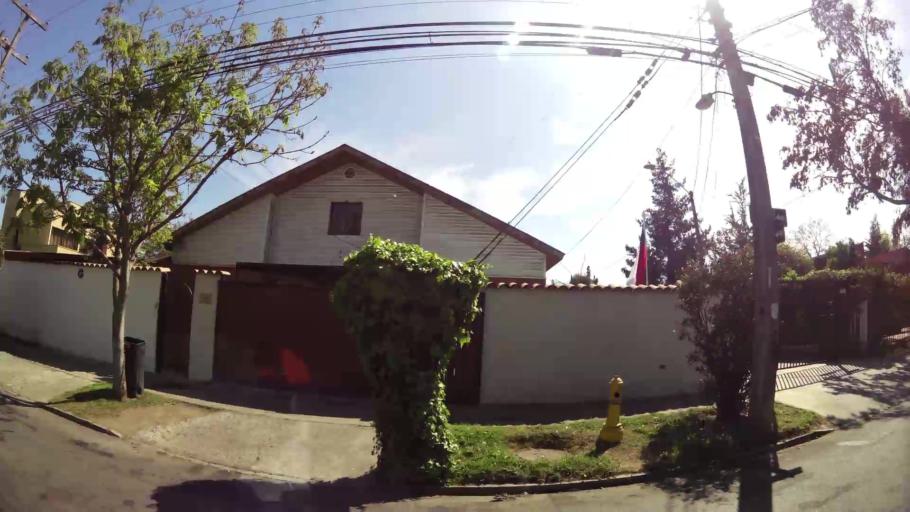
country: CL
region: Santiago Metropolitan
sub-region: Provincia de Santiago
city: Villa Presidente Frei, Nunoa, Santiago, Chile
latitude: -33.4461
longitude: -70.5500
